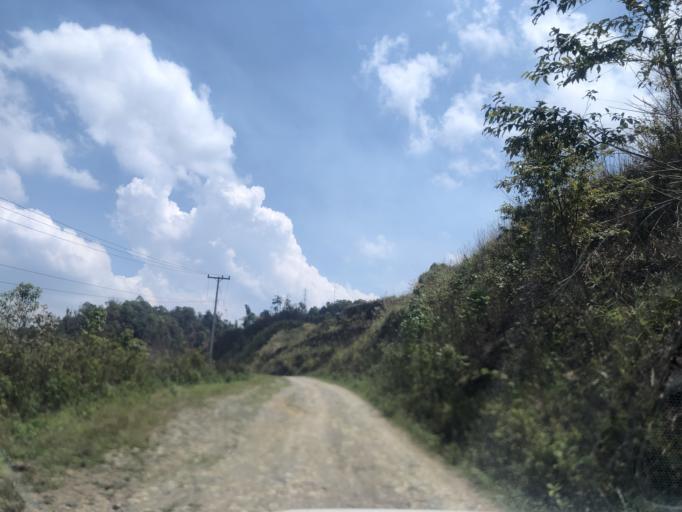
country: LA
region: Phongsali
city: Phongsali
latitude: 21.4014
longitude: 102.1889
